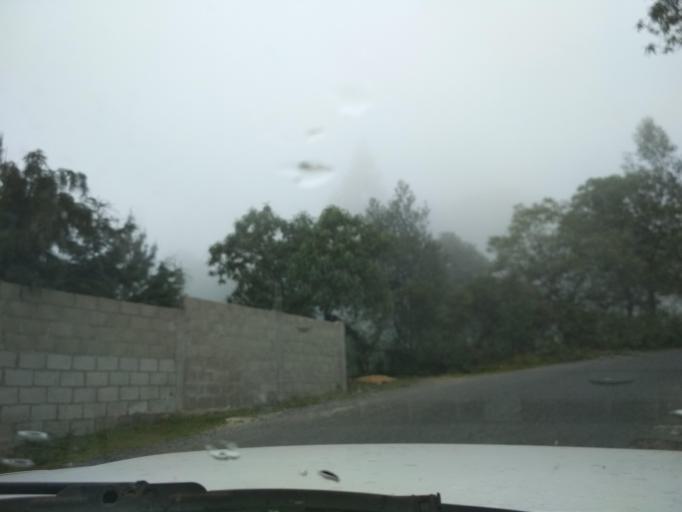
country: MX
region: Veracruz
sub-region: Mariano Escobedo
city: Loma Grande
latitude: 18.9340
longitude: -97.2210
